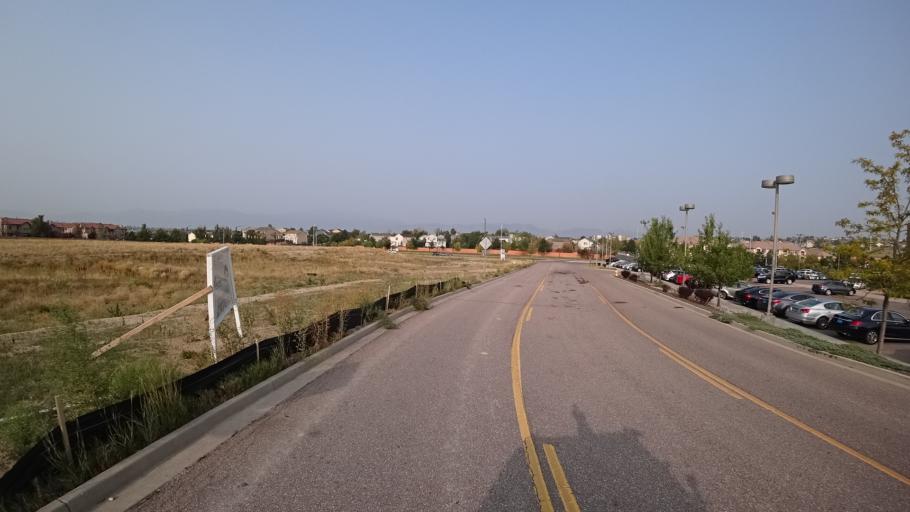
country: US
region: Colorado
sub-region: El Paso County
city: Black Forest
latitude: 38.9369
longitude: -104.7382
